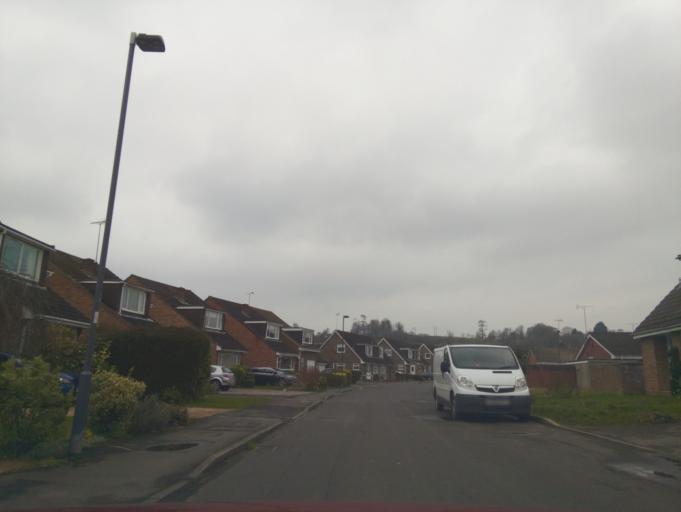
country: GB
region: England
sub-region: South Gloucestershire
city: Charfield
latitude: 51.6253
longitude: -2.4032
